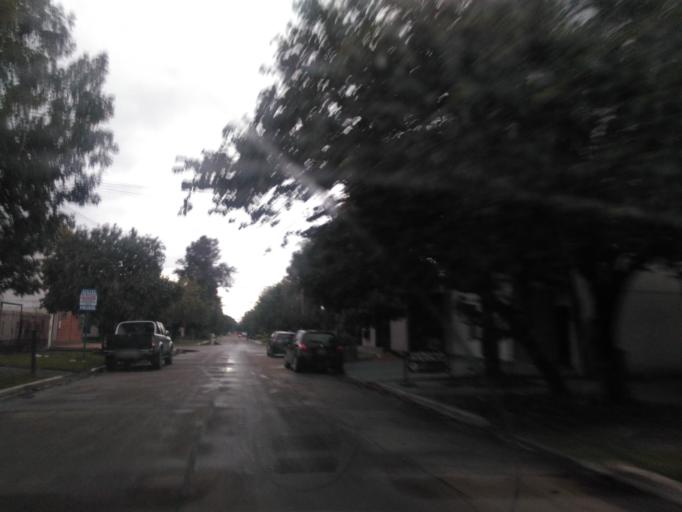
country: AR
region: Chaco
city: Resistencia
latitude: -27.4629
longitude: -58.9961
